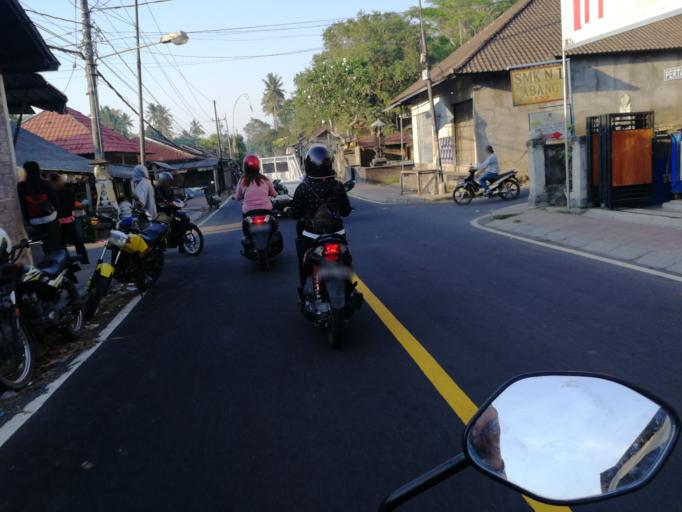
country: ID
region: Bali
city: Tistagede
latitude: -8.3787
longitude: 115.6092
